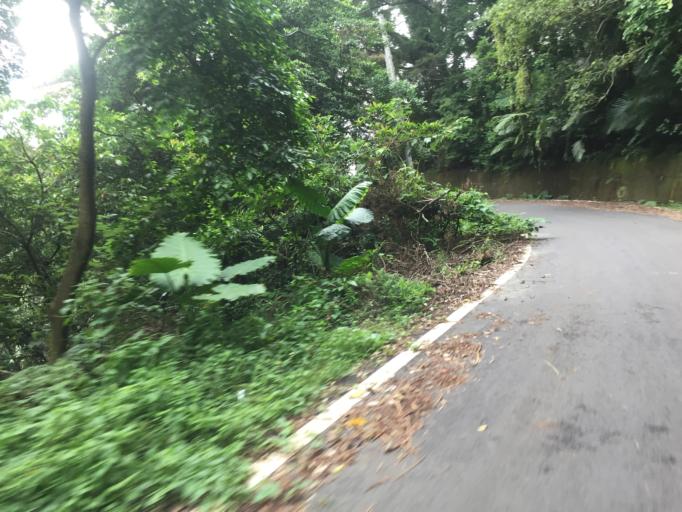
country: TW
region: Taiwan
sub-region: Hsinchu
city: Zhubei
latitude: 24.7875
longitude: 121.1565
